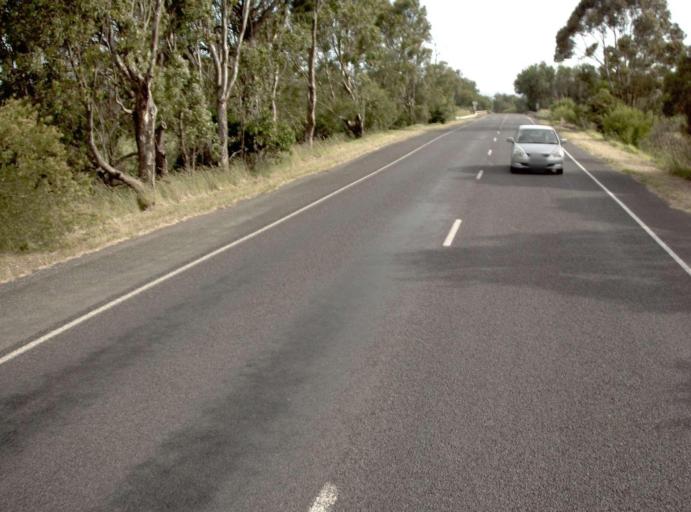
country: AU
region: Victoria
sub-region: Latrobe
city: Traralgon
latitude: -38.1512
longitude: 146.5544
